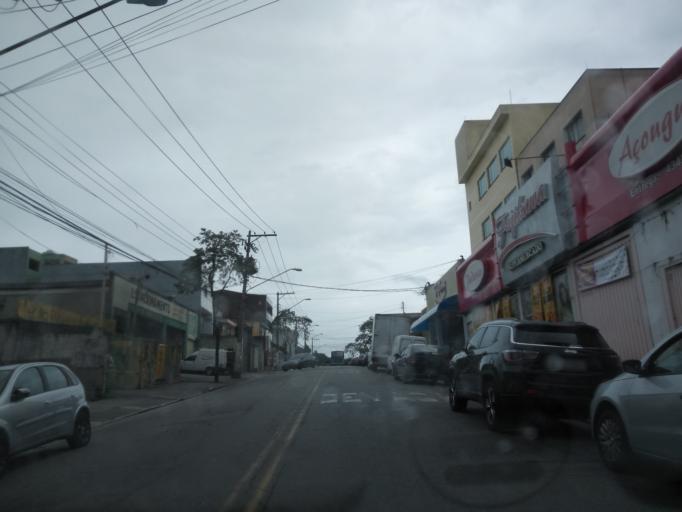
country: BR
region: Sao Paulo
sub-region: Sao Bernardo Do Campo
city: Sao Bernardo do Campo
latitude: -23.6994
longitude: -46.5810
